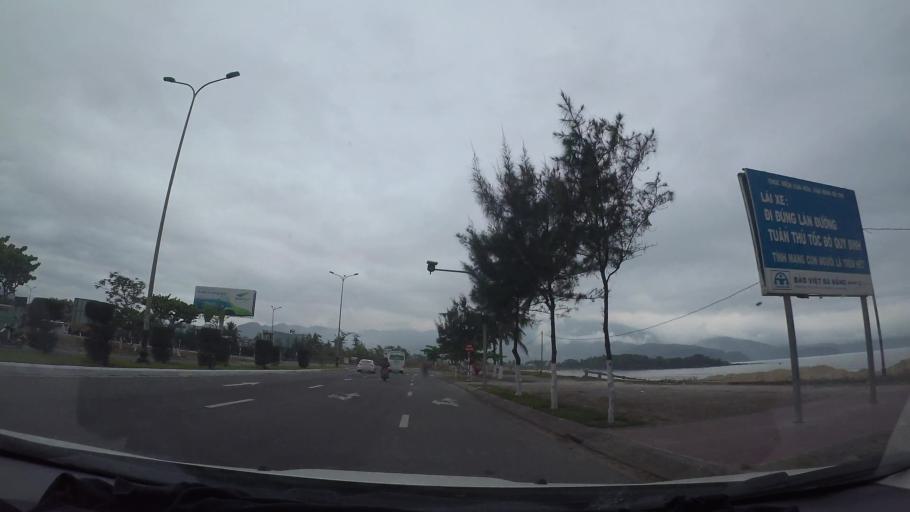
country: VN
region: Da Nang
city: Lien Chieu
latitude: 16.1101
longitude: 108.1330
